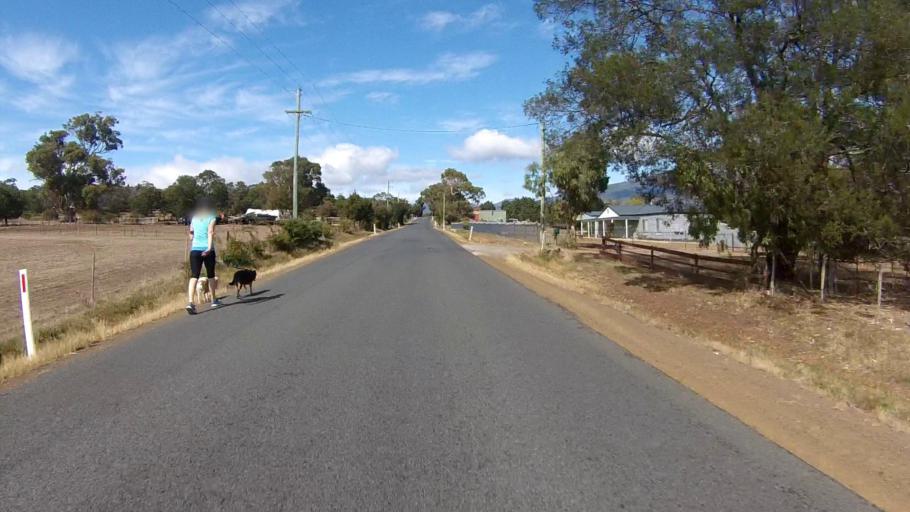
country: AU
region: Tasmania
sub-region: Brighton
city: Old Beach
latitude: -42.7660
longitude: 147.2756
